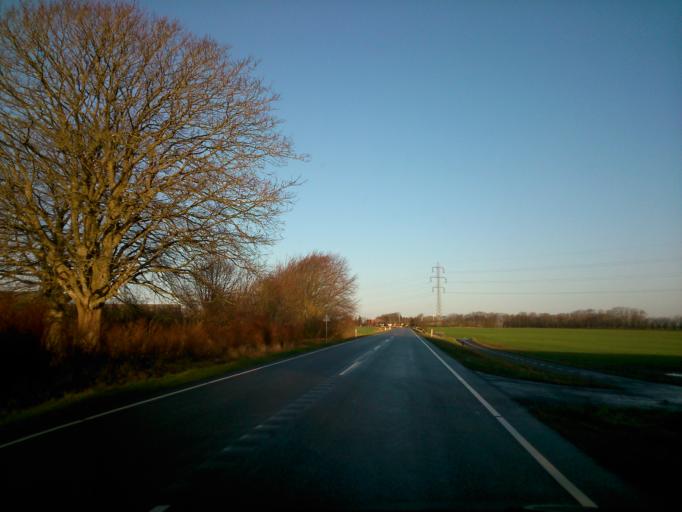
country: DK
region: Central Jutland
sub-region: Ringkobing-Skjern Kommune
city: Tarm
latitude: 55.9795
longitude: 8.5881
